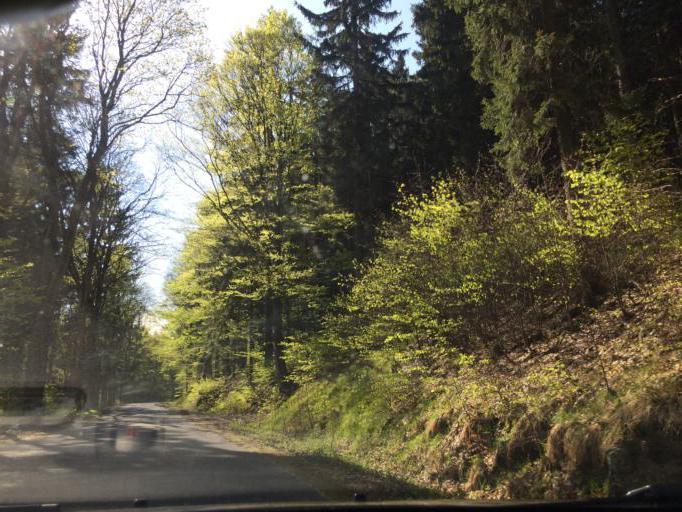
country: PL
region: Lower Silesian Voivodeship
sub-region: Powiat klodzki
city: Jugow
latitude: 50.6667
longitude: 16.5200
